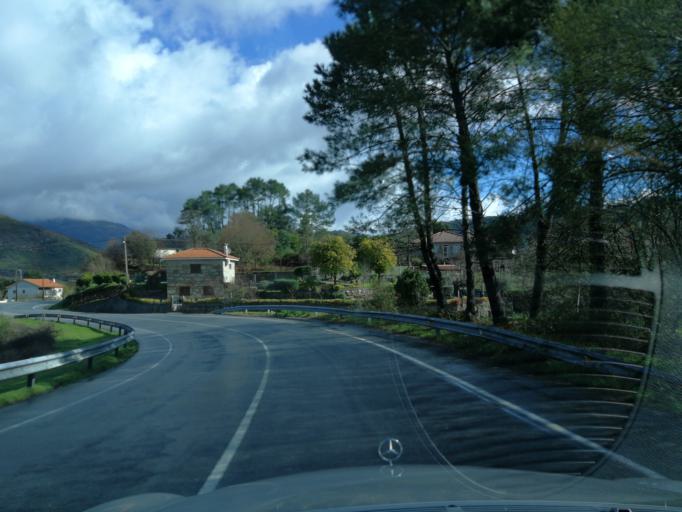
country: PT
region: Braga
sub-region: Terras de Bouro
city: Antas
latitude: 41.8377
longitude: -8.2953
